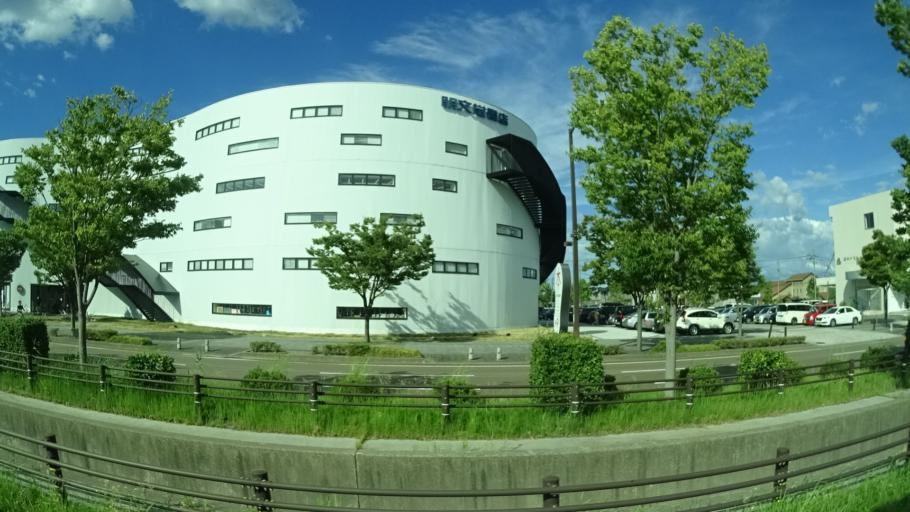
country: JP
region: Ishikawa
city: Kanazawa-shi
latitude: 36.5985
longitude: 136.6235
